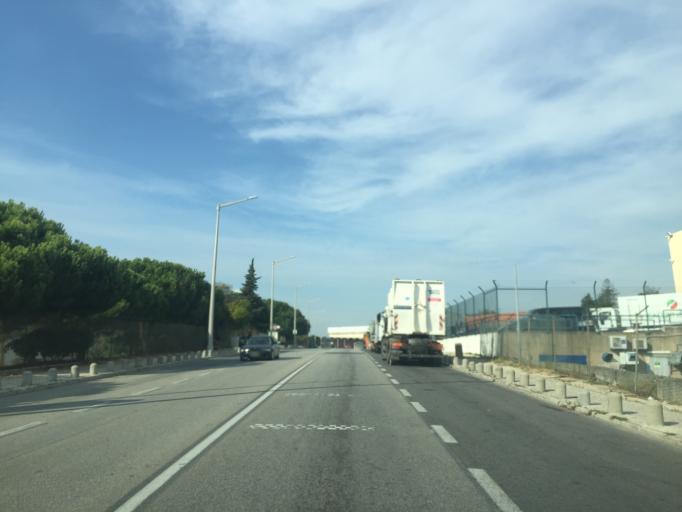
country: PT
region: Lisbon
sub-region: Loures
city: Sacavem
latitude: 38.7764
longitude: -9.1266
